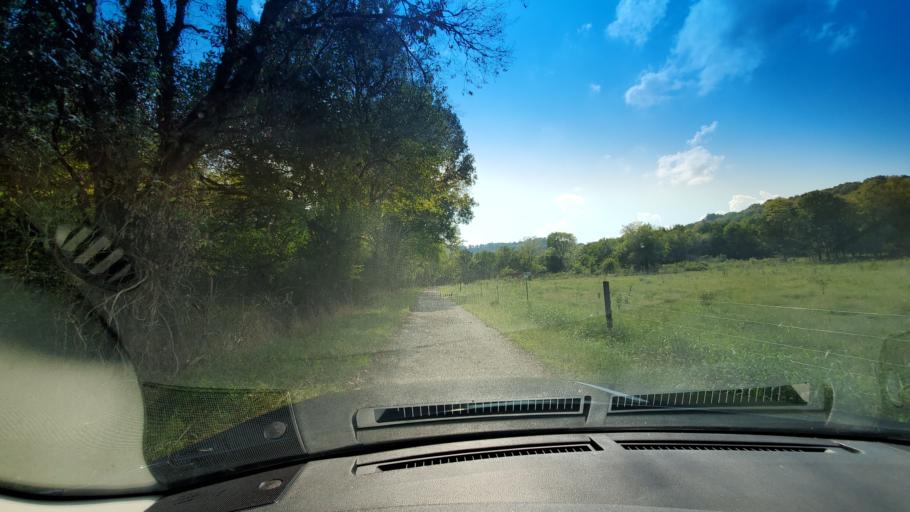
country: US
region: Tennessee
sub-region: Smith County
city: South Carthage
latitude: 36.2288
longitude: -85.9900
